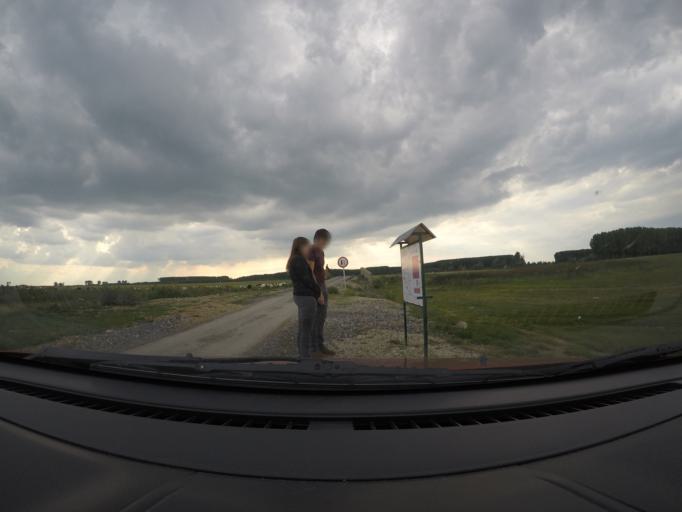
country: RS
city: Uzdin
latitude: 45.2031
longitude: 20.5939
